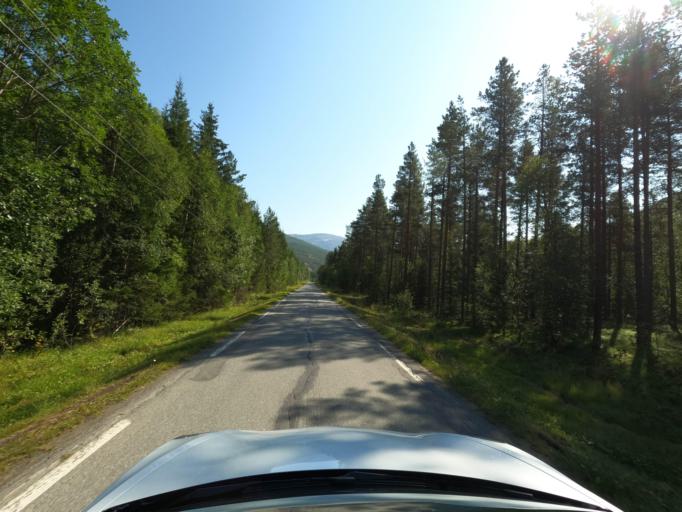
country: NO
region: Nordland
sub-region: Narvik
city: Narvik
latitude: 68.1993
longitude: 17.5491
